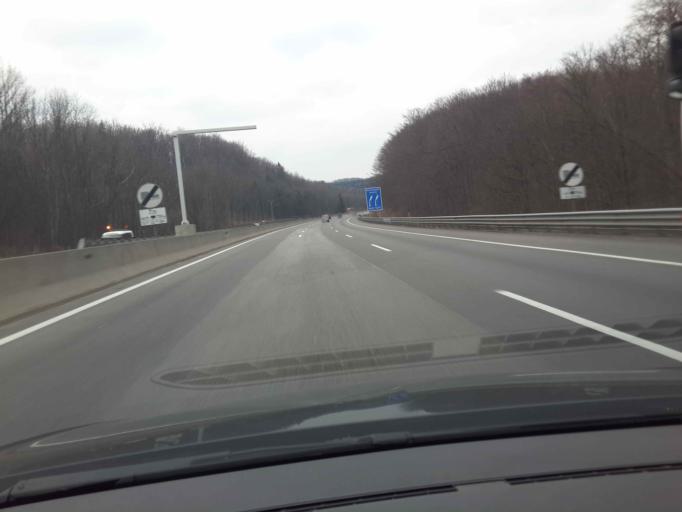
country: AT
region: Lower Austria
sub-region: Politischer Bezirk Baden
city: Klausen-Leopoldsdorf
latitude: 48.1133
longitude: 15.9744
